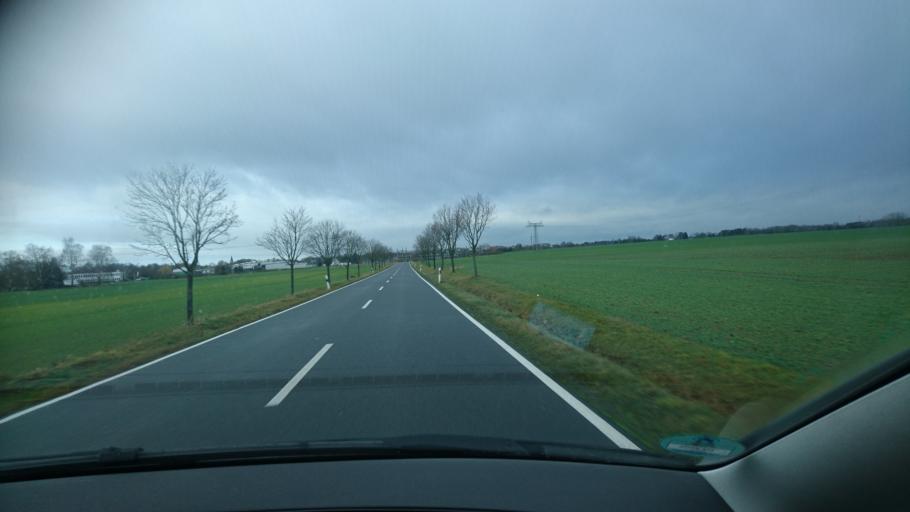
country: DE
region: Saxony
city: Bad Duben
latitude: 51.5881
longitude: 12.6133
